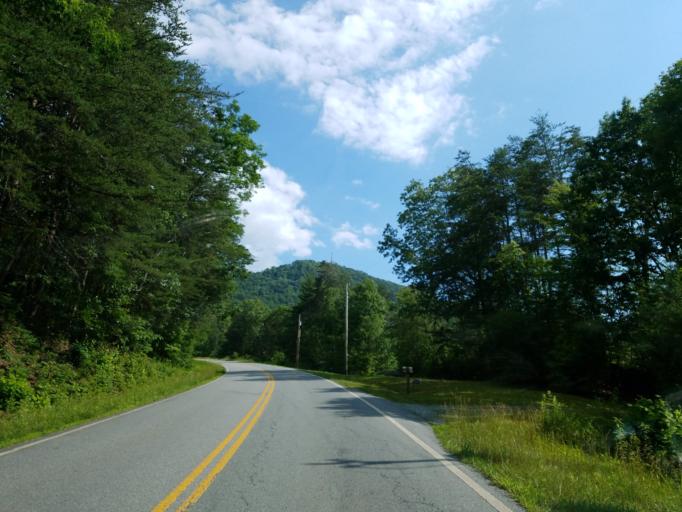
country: US
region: Georgia
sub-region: Fannin County
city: Blue Ridge
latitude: 34.8253
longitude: -84.3055
